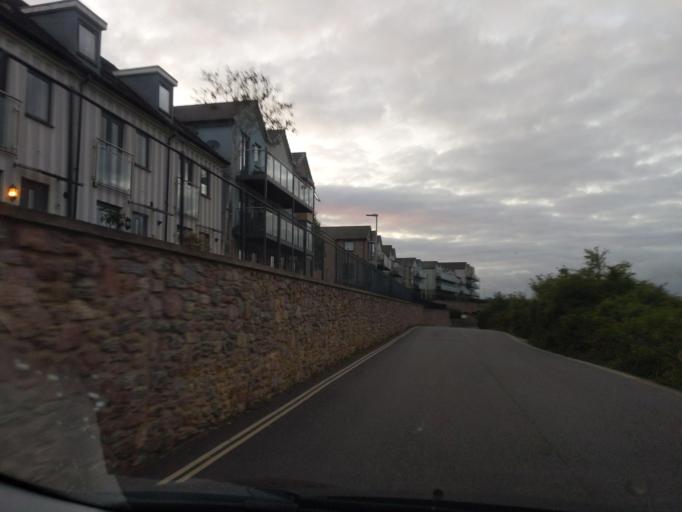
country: GB
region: England
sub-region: Plymouth
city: Plymstock
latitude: 50.3565
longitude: -4.1131
